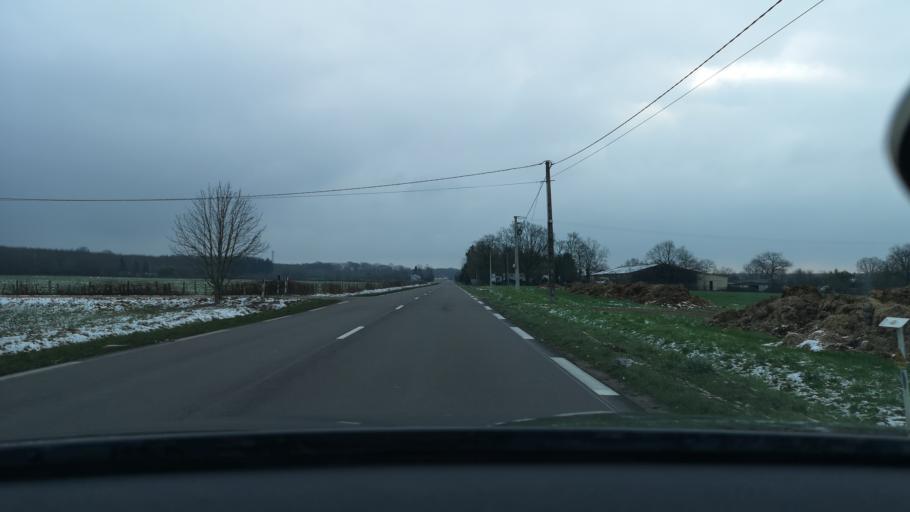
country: FR
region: Bourgogne
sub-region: Departement de Saone-et-Loire
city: Ouroux-sur-Saone
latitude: 46.7730
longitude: 4.9666
